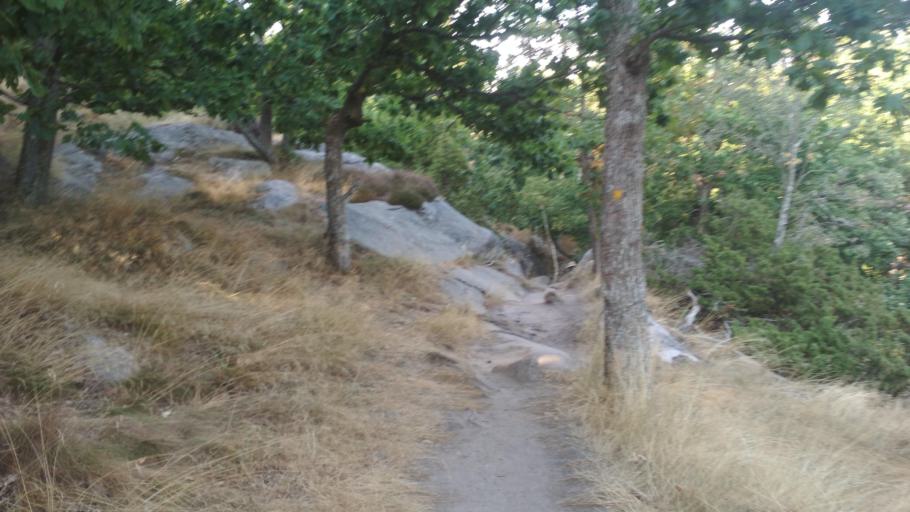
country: DK
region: Capital Region
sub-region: Bornholm Kommune
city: Akirkeby
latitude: 55.1093
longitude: 14.9000
